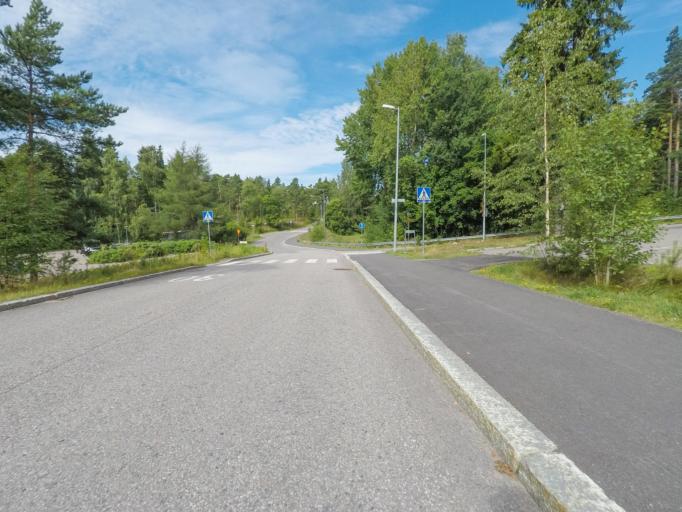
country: FI
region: Uusimaa
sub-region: Helsinki
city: Vantaa
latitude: 60.1617
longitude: 25.0836
